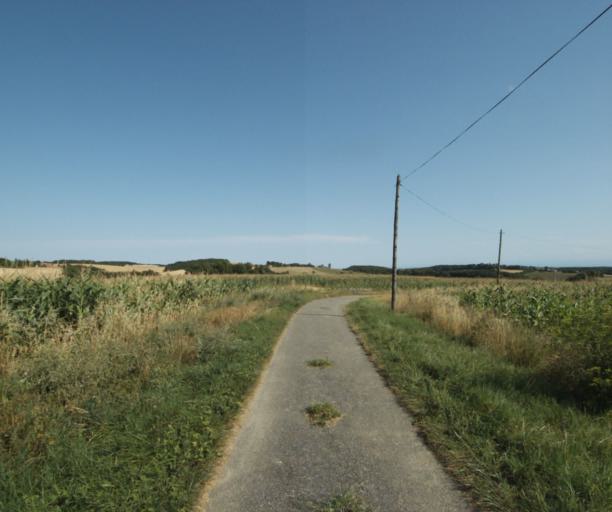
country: FR
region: Midi-Pyrenees
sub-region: Departement de la Haute-Garonne
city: Avignonet-Lauragais
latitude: 43.4266
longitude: 1.8239
